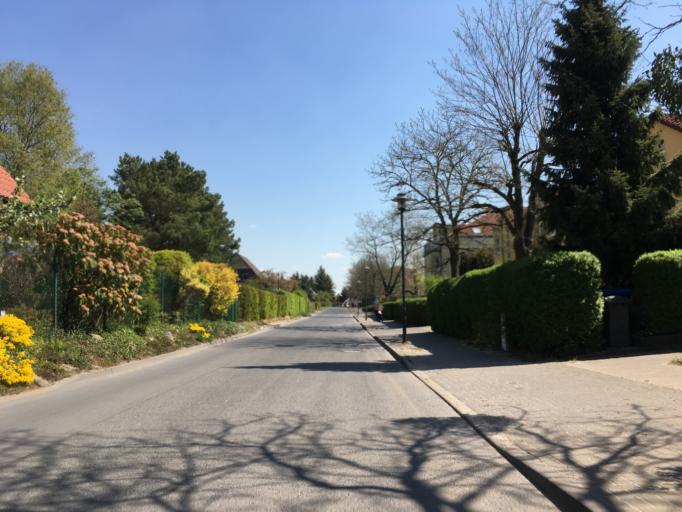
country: DE
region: Brandenburg
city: Bernau bei Berlin
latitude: 52.6724
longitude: 13.5519
